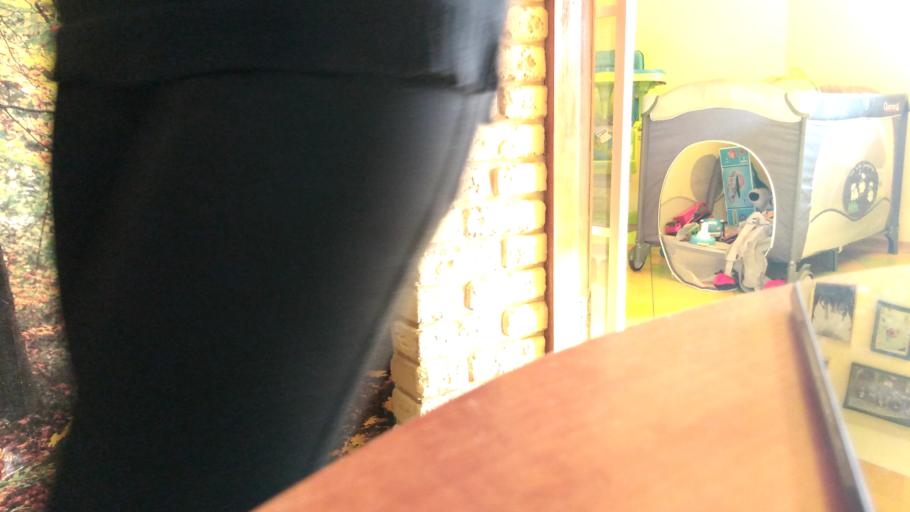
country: RU
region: Tverskaya
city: Radchenko
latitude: 56.6925
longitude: 36.4340
